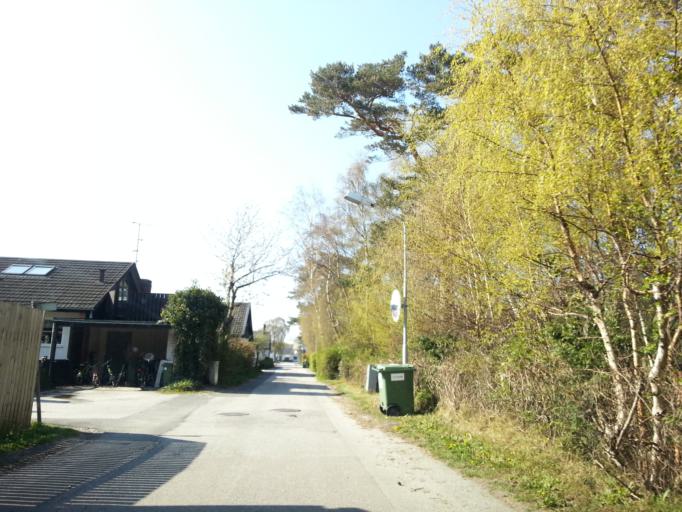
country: SE
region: Skane
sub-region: Vellinge Kommun
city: Hollviken
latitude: 55.4192
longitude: 12.9577
